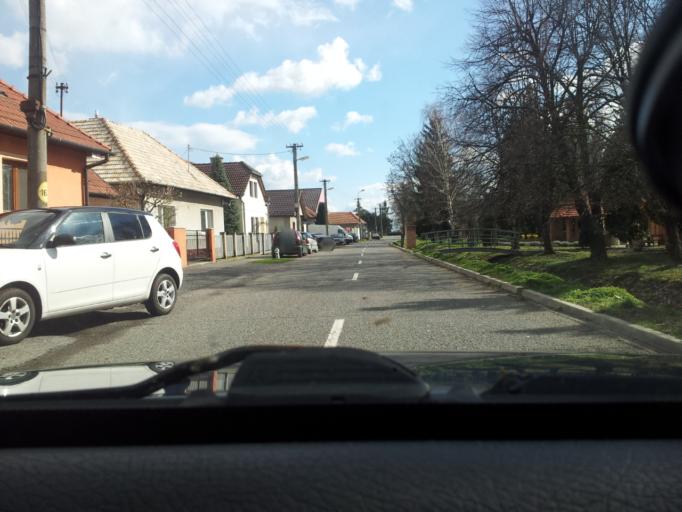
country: SK
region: Nitriansky
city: Tlmace
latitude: 48.2910
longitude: 18.5620
